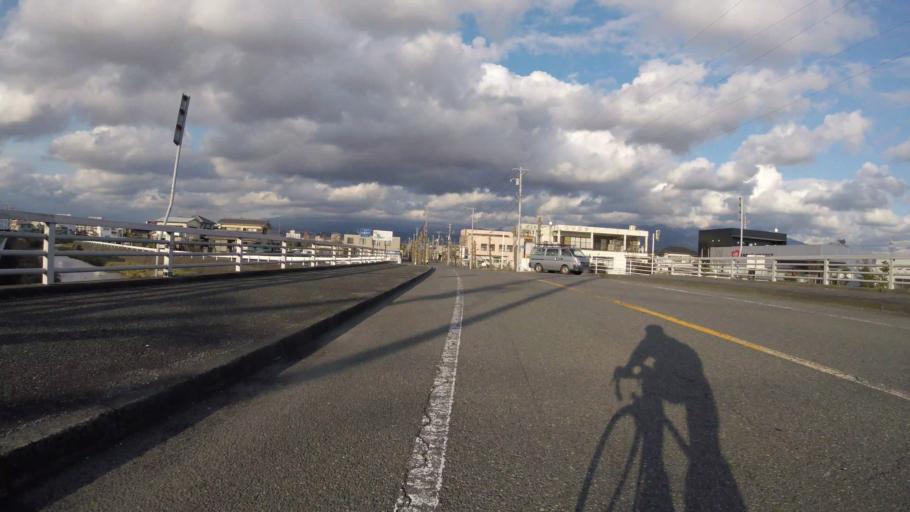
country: JP
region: Shizuoka
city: Fuji
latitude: 35.1519
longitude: 138.6824
